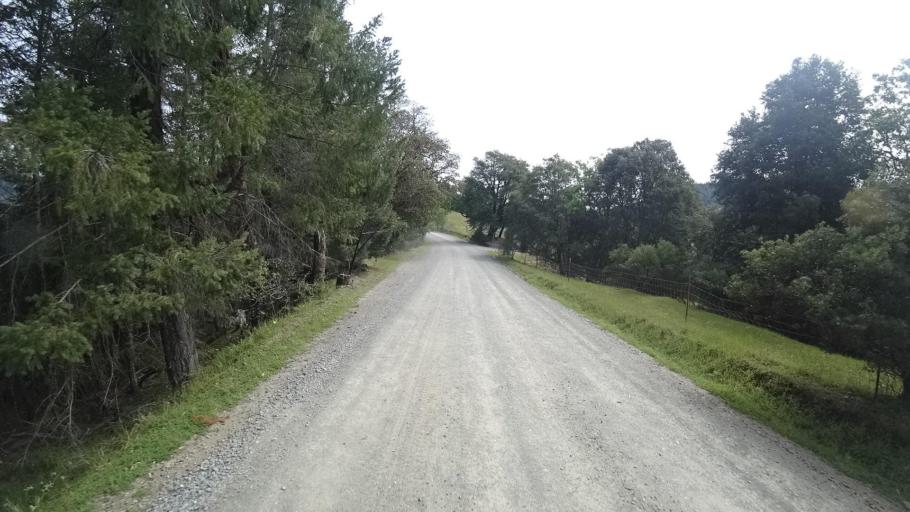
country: US
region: California
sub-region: Humboldt County
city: Redway
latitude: 40.0559
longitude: -123.8354
